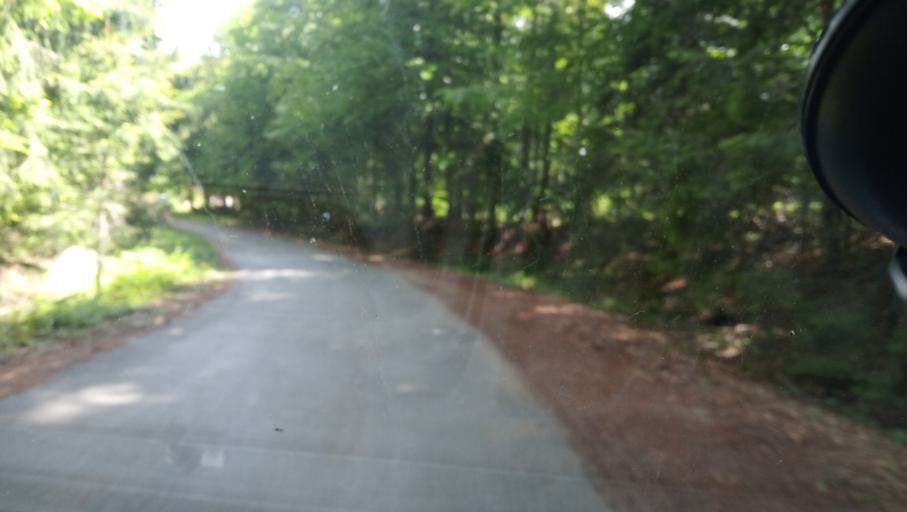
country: RO
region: Caras-Severin
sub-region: Comuna Valiug
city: Valiug
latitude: 45.2230
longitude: 22.0727
